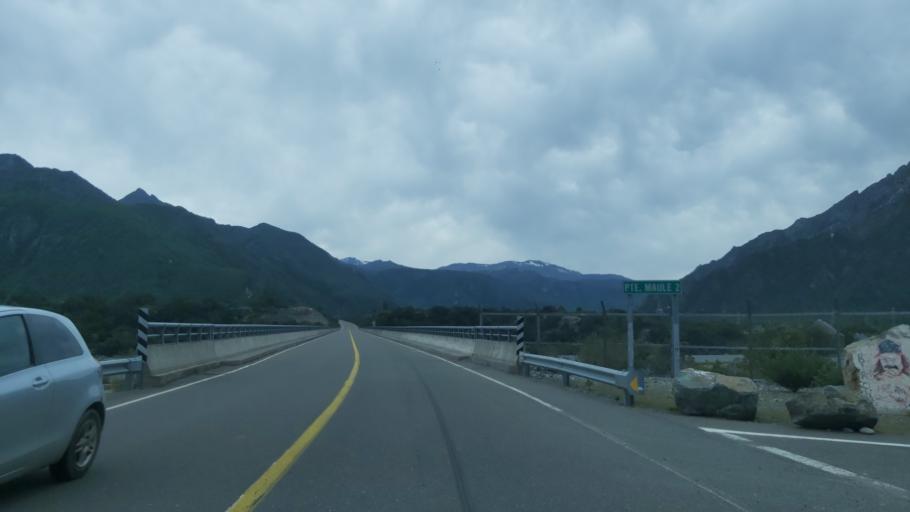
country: CL
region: Maule
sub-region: Provincia de Linares
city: Colbun
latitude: -35.7098
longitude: -71.0787
